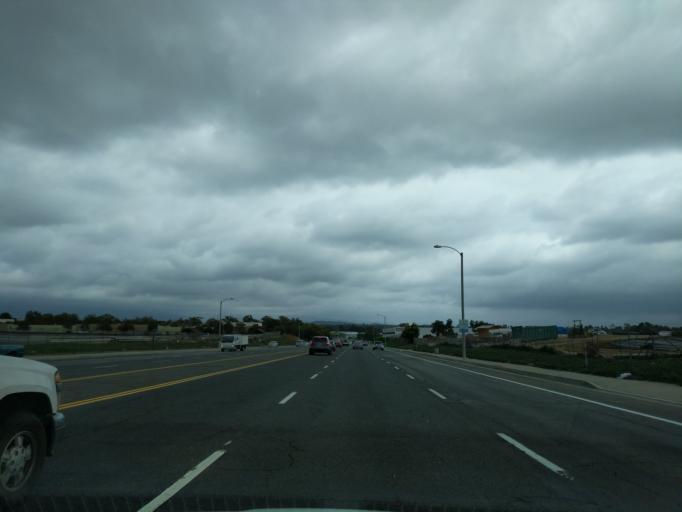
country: US
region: California
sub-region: Orange County
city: Laguna Woods
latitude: 33.6387
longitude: -117.7269
